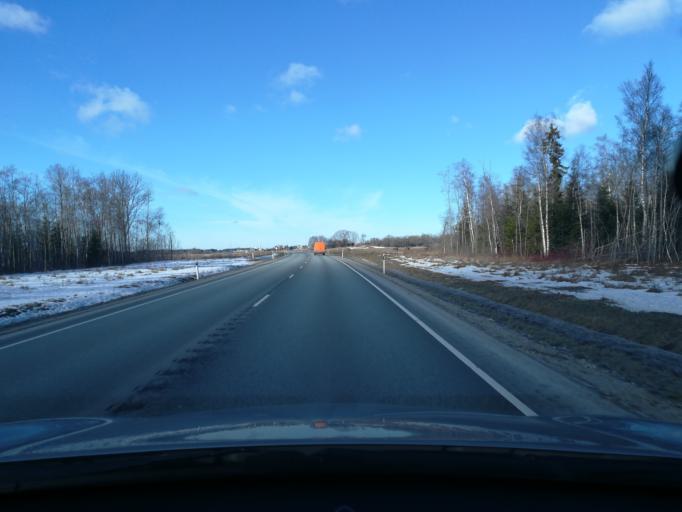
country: EE
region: Harju
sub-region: Saku vald
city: Saku
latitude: 59.3262
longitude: 24.6363
